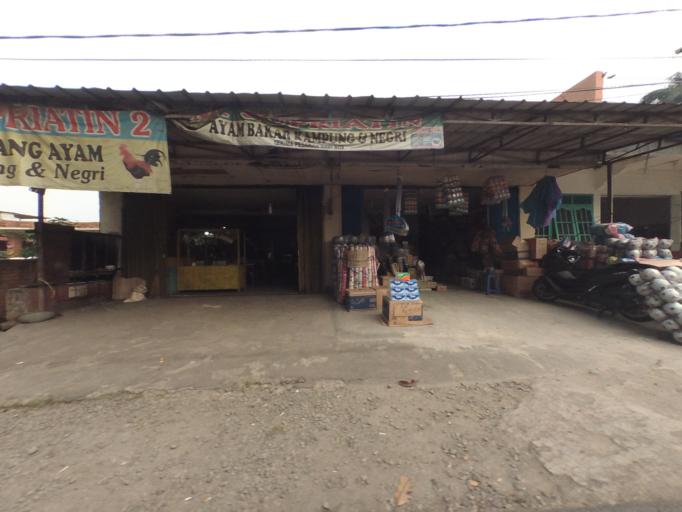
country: ID
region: West Java
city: Ciampea
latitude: -6.5556
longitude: 106.6959
